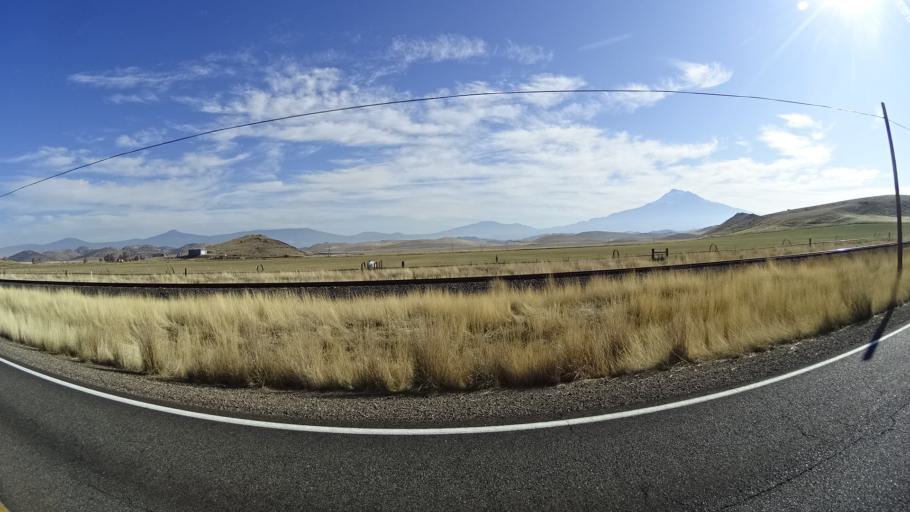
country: US
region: California
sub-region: Siskiyou County
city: Montague
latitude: 41.5581
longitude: -122.5268
